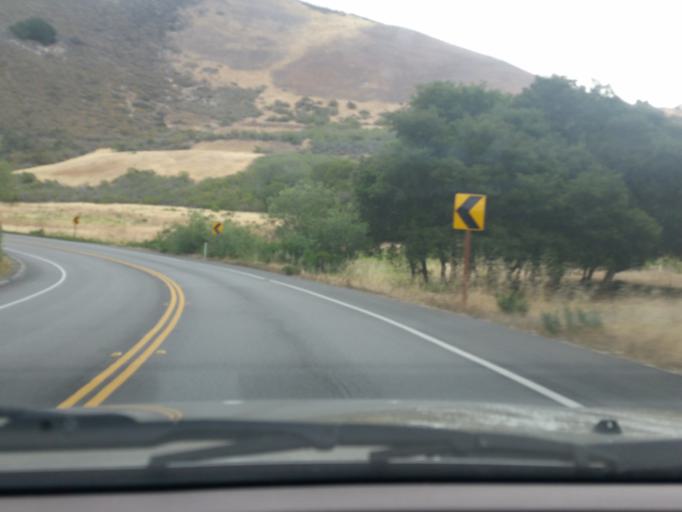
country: US
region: California
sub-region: San Luis Obispo County
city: Avila Beach
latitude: 35.1797
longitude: -120.7246
